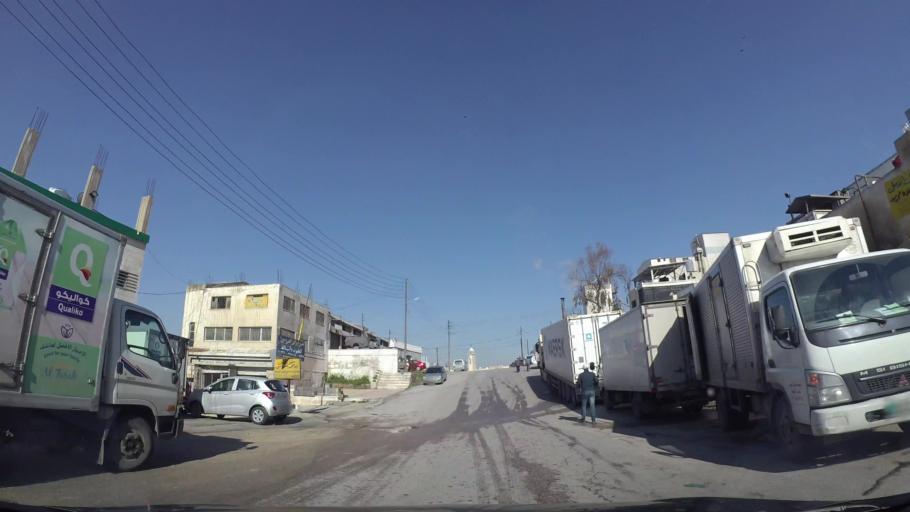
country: JO
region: Zarqa
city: Russeifa
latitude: 31.9869
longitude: 35.9967
